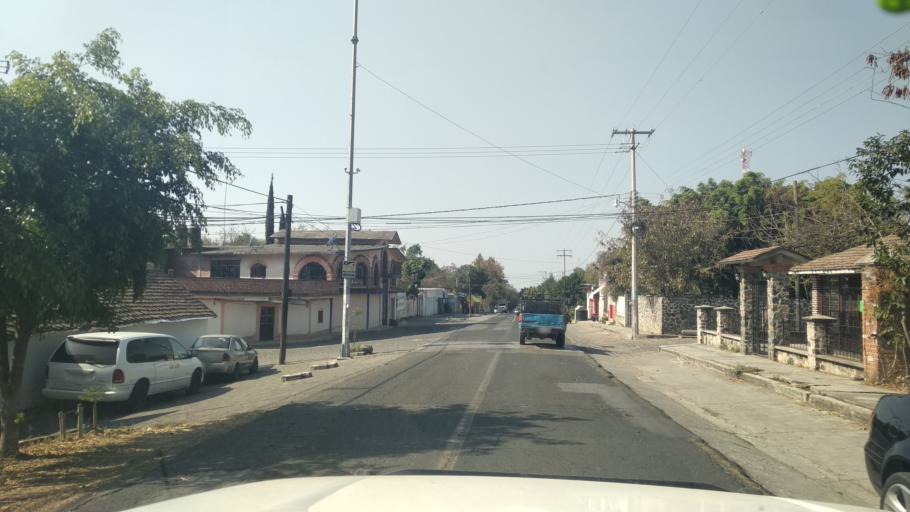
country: MX
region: Morelos
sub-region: Zacualpan
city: Zacualpan de Amilpas
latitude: 18.7893
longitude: -98.7687
